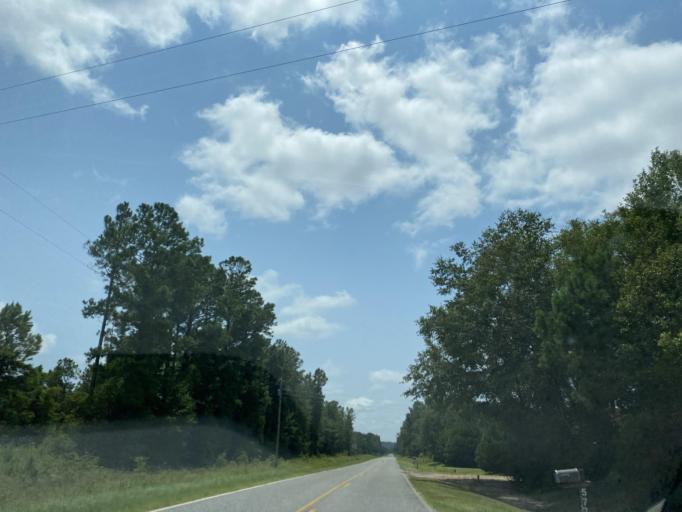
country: US
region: Georgia
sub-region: Telfair County
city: Lumber City
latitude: 31.9798
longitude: -82.7024
